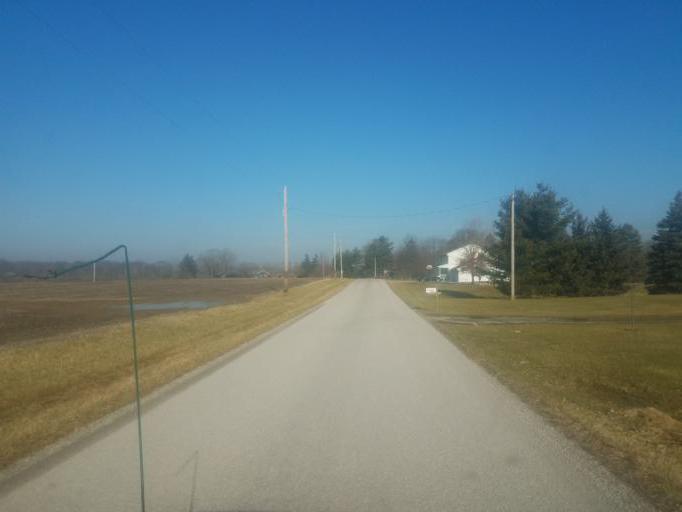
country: US
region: Ohio
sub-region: Seneca County
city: Tiffin
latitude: 41.1231
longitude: -83.1120
